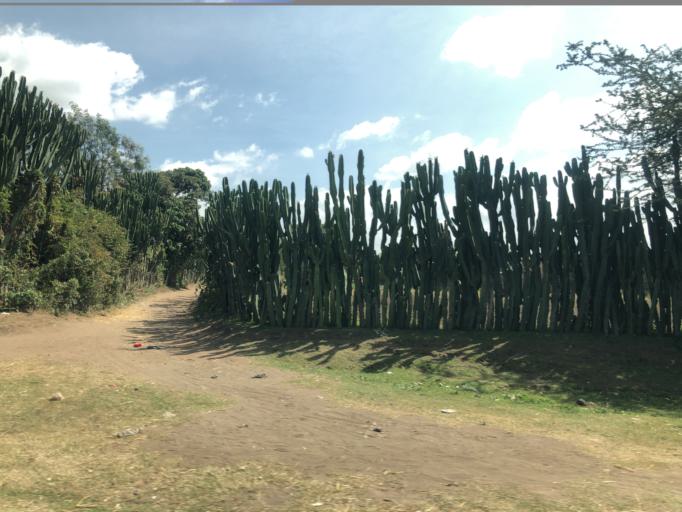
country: ET
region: Oromiya
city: Shashemene
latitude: 7.2300
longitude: 38.6324
